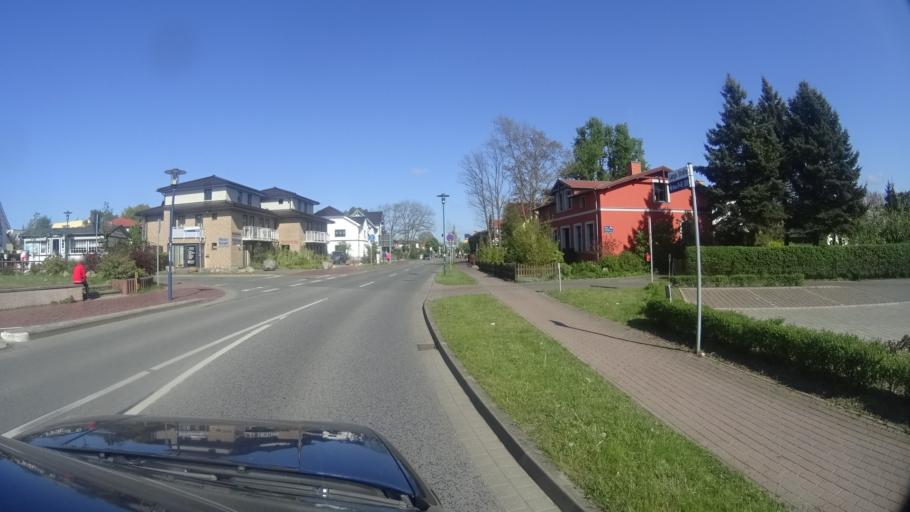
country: DE
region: Mecklenburg-Vorpommern
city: Seeheilbad Graal-Muritz
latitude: 54.2492
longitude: 12.2361
